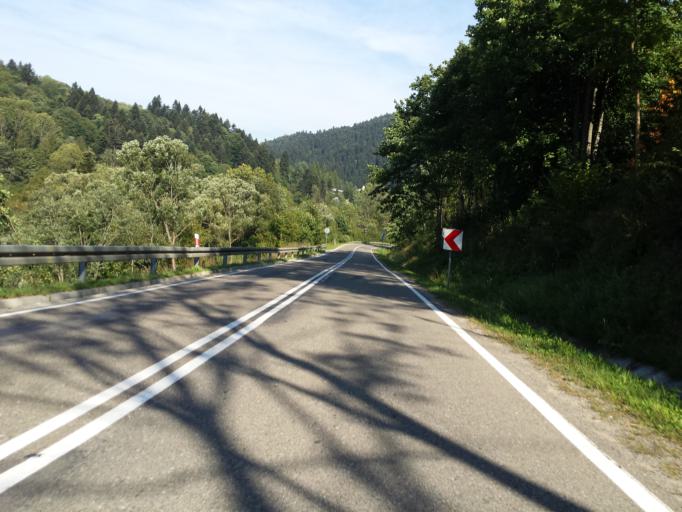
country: PL
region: Subcarpathian Voivodeship
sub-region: Powiat leski
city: Baligrod
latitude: 49.3104
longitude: 22.2773
